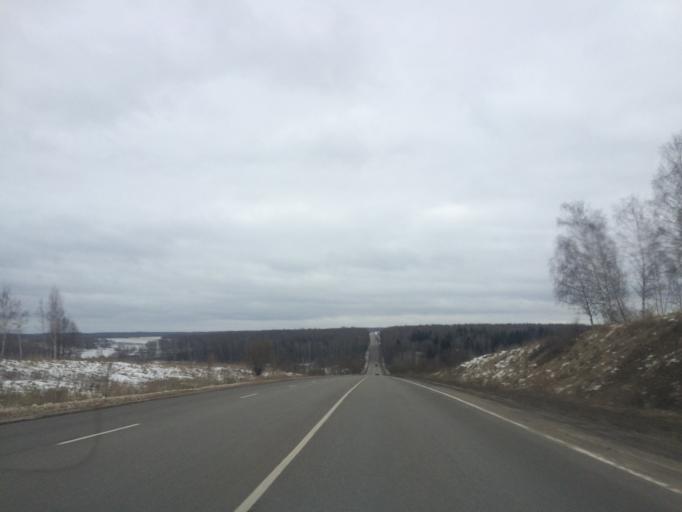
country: RU
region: Tula
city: Barsuki
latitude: 54.1504
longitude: 37.4072
